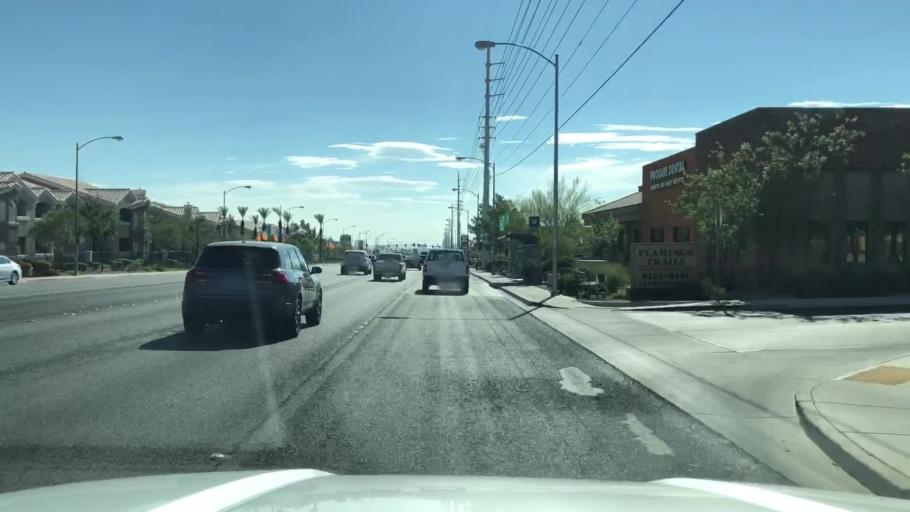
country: US
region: Nevada
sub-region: Clark County
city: Summerlin South
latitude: 36.1149
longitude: -115.2921
